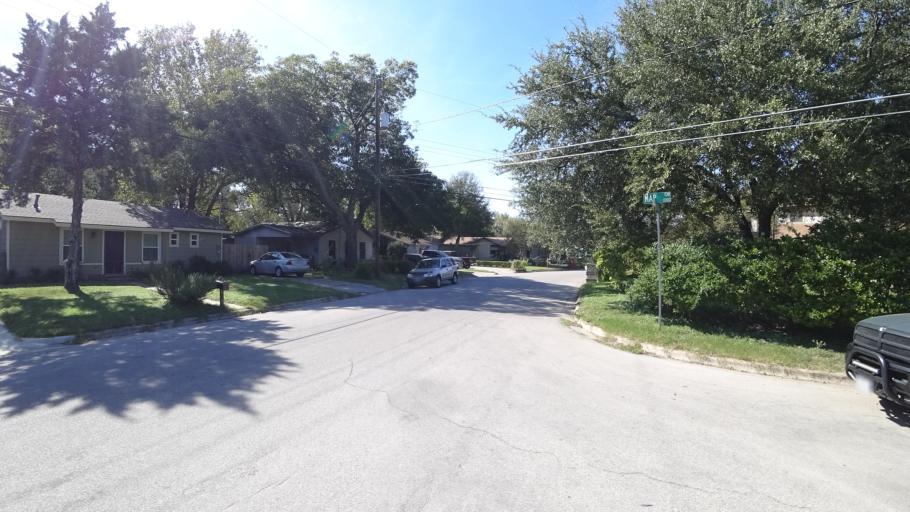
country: US
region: Texas
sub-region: Travis County
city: Austin
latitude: 30.2691
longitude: -97.6918
